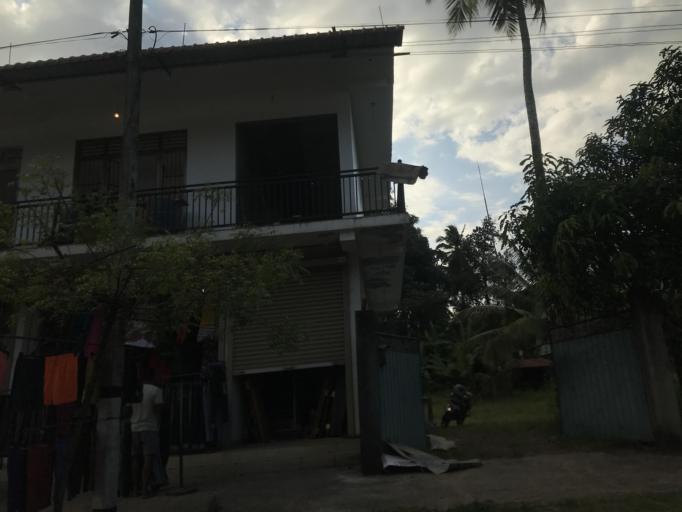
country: LK
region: Western
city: Gampaha
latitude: 7.0800
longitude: 79.9871
